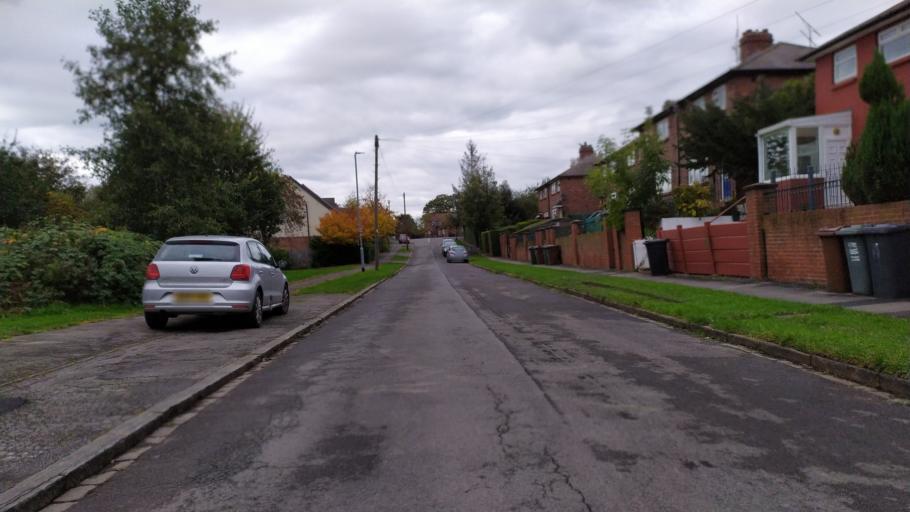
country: GB
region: England
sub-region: City and Borough of Leeds
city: Chapel Allerton
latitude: 53.8230
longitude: -1.5505
